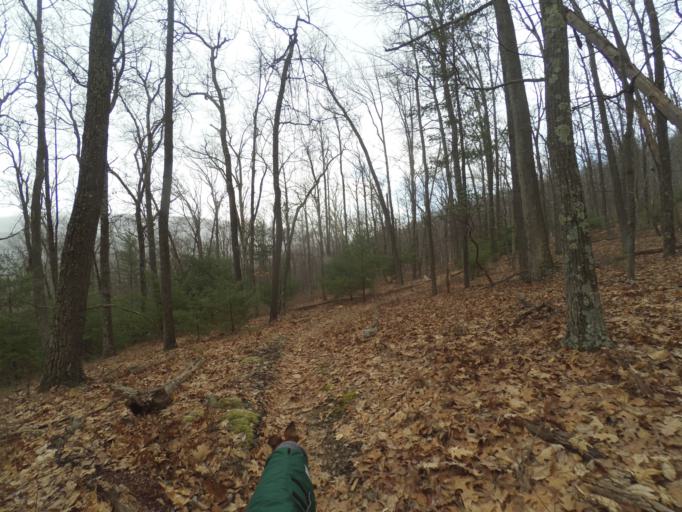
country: US
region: Pennsylvania
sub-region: Centre County
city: Centre Hall
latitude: 40.7675
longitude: -77.7010
